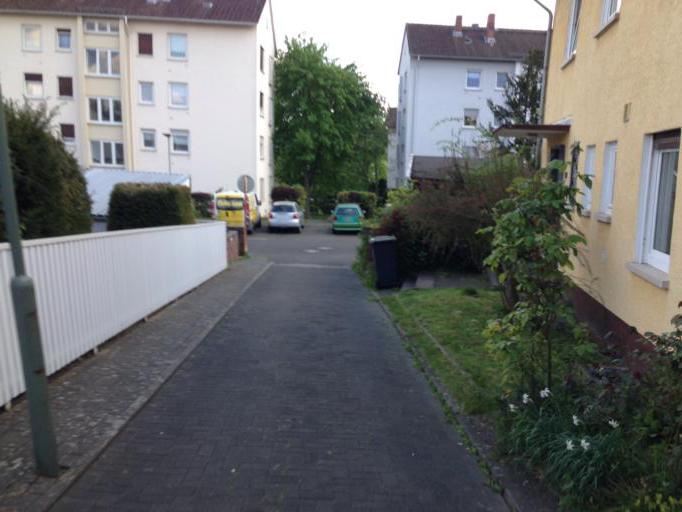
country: DE
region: Hesse
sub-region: Regierungsbezirk Giessen
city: Giessen
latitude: 50.6001
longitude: 8.6931
